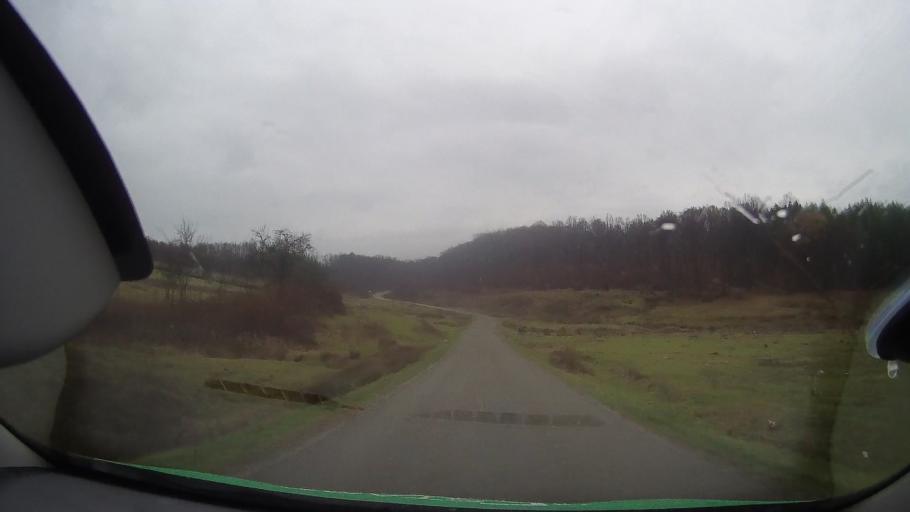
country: RO
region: Bihor
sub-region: Comuna Rabagani
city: Rabagani
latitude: 46.7206
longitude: 22.2318
